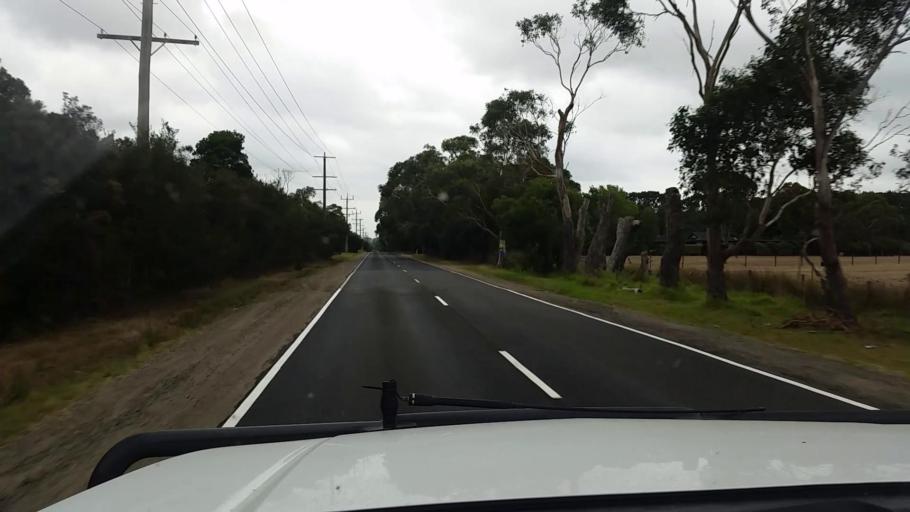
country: AU
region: Victoria
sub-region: Mornington Peninsula
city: Somerville
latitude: -38.2133
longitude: 145.1567
